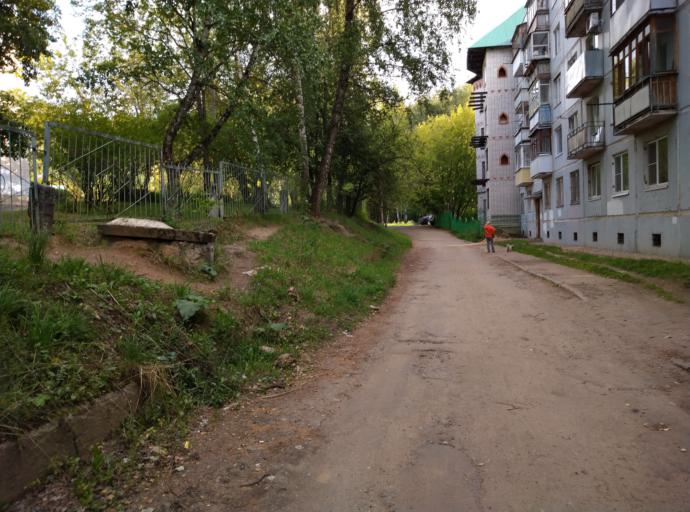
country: RU
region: Kostroma
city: Oktyabr'skiy
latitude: 57.7615
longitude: 40.9713
